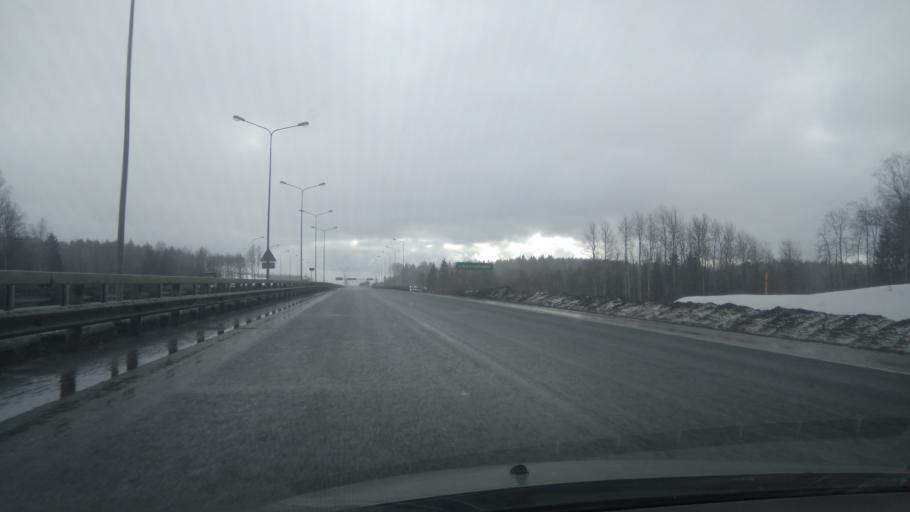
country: RU
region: Perm
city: Zvezdnyy
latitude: 57.7407
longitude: 56.3390
